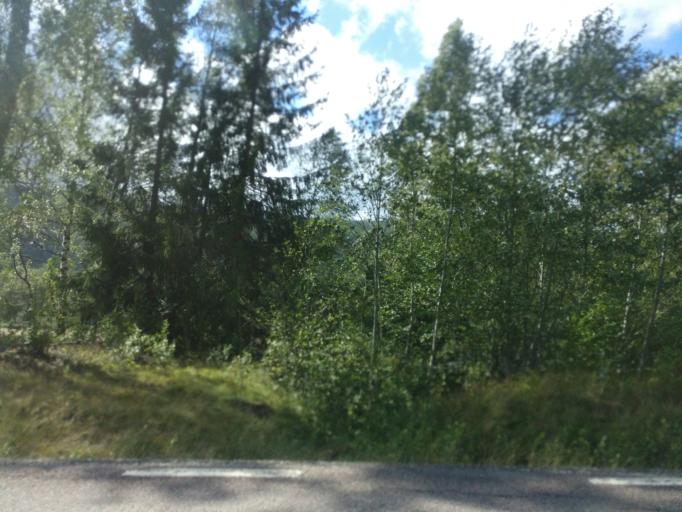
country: SE
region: Vaermland
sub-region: Hagfors Kommun
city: Ekshaerad
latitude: 60.3665
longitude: 13.3081
